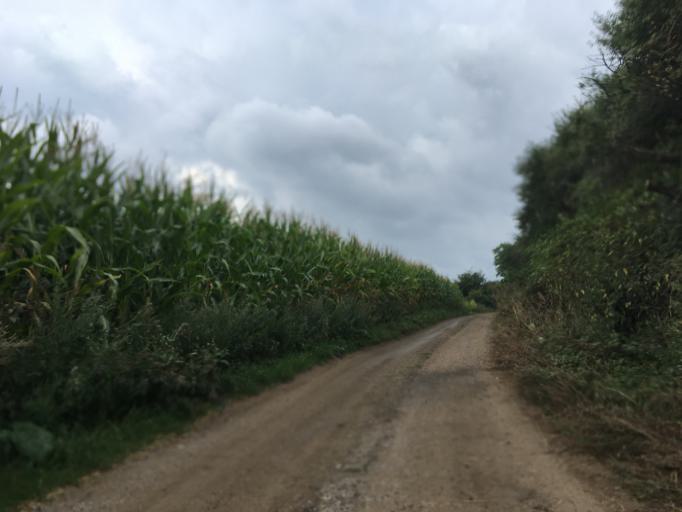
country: DE
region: Brandenburg
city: Angermunde
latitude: 52.9741
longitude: 13.9516
